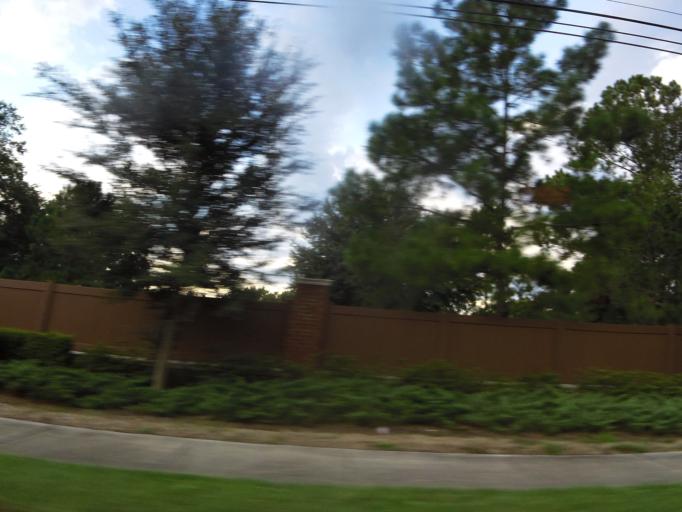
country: US
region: Florida
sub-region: Clay County
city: Bellair-Meadowbrook Terrace
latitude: 30.2981
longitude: -81.7833
